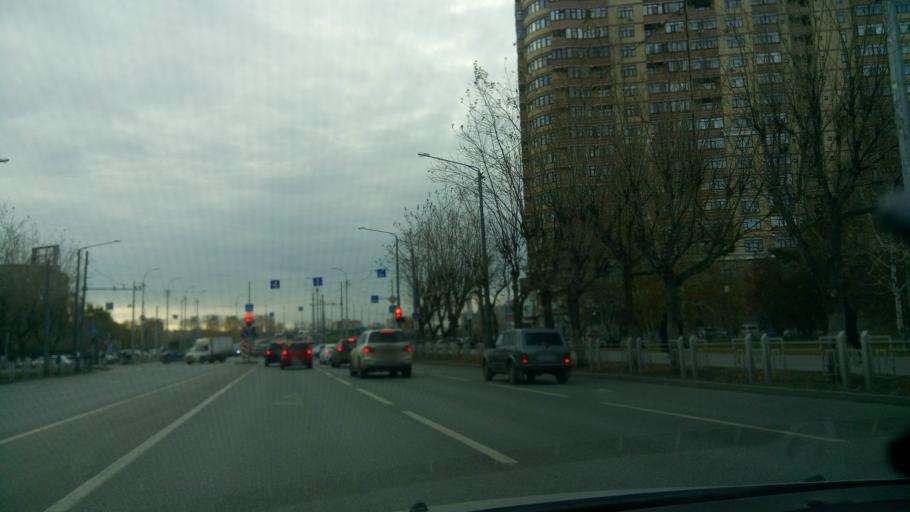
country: RU
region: Tjumen
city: Tyumen
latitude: 57.1354
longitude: 65.5657
